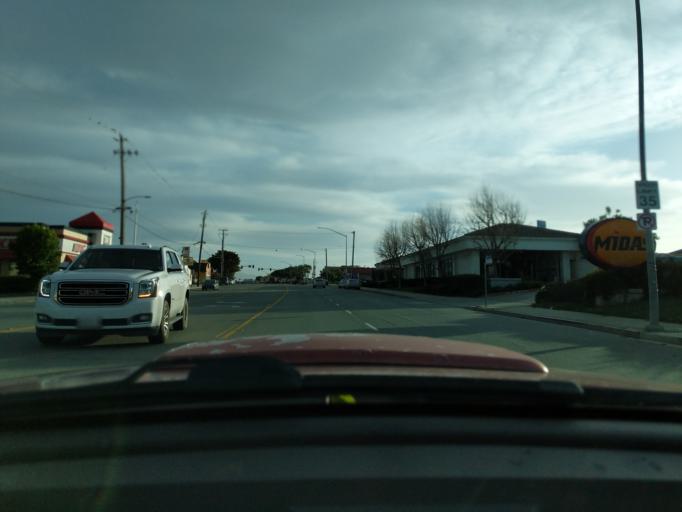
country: US
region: California
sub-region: Monterey County
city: Boronda
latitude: 36.7237
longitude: -121.6564
